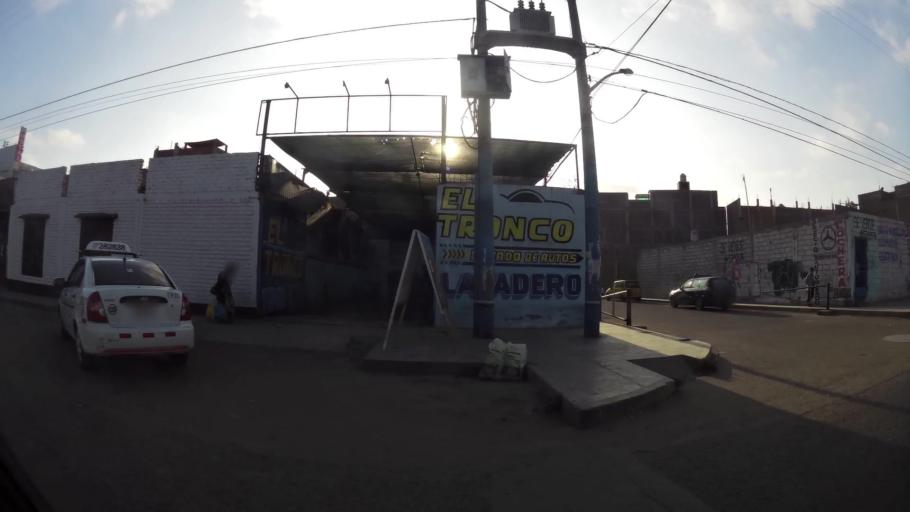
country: PE
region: La Libertad
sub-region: Provincia de Trujillo
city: El Porvenir
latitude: -8.0887
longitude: -79.0028
